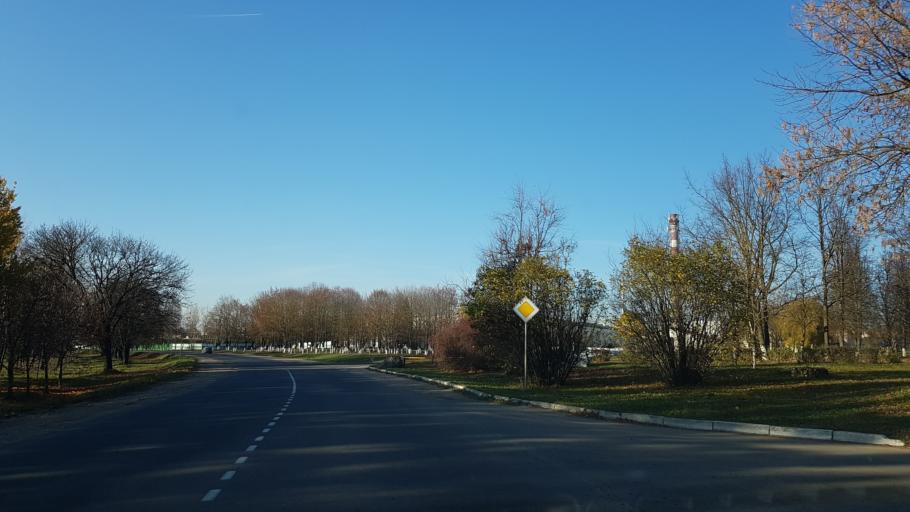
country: BY
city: Fanipol
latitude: 53.7338
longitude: 27.3306
